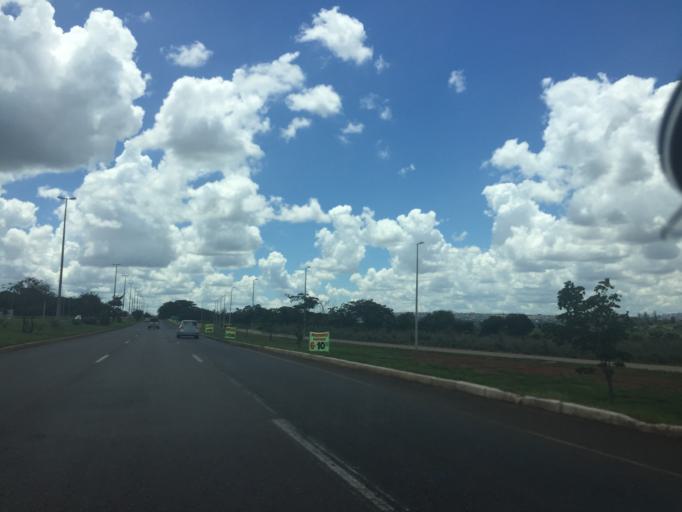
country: BR
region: Federal District
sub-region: Brasilia
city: Brasilia
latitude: -15.8632
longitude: -47.9385
